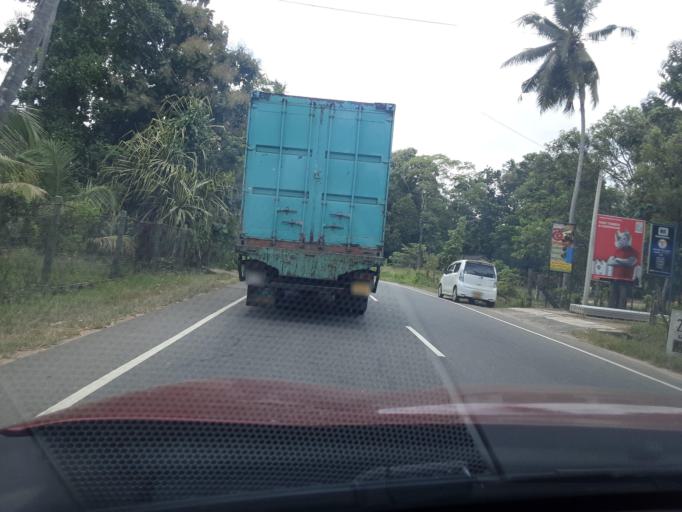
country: LK
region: North Western
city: Kuliyapitiya
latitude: 7.4469
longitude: 80.2020
